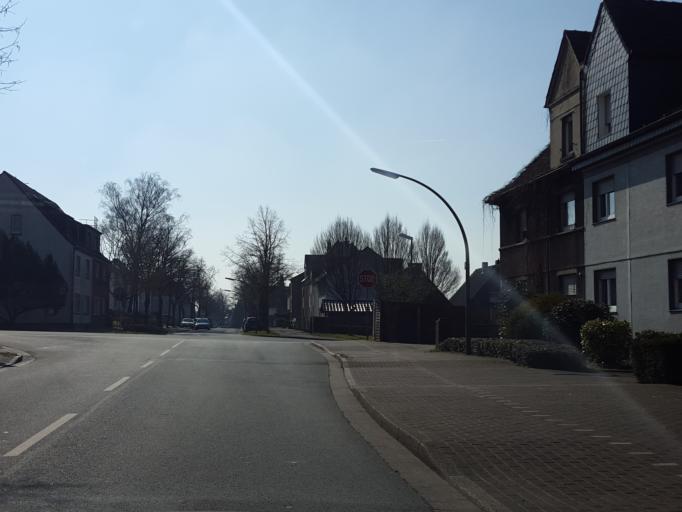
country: DE
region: North Rhine-Westphalia
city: Oer-Erkenschwick
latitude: 51.6511
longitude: 7.2473
